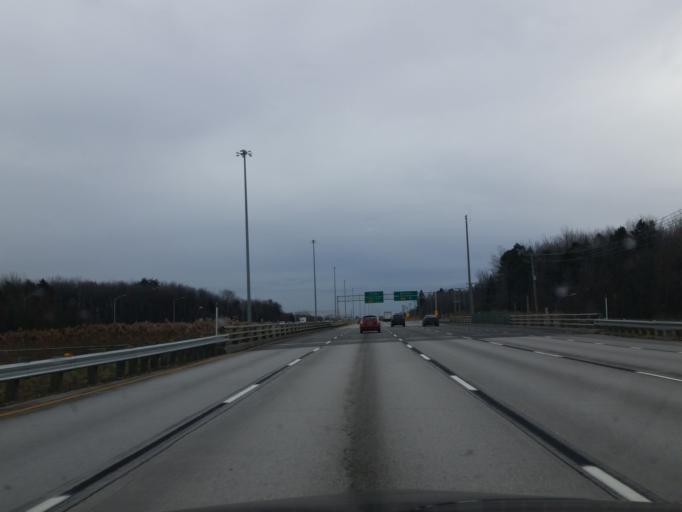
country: CA
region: Quebec
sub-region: Laurentides
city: Blainville
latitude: 45.6585
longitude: -73.8864
